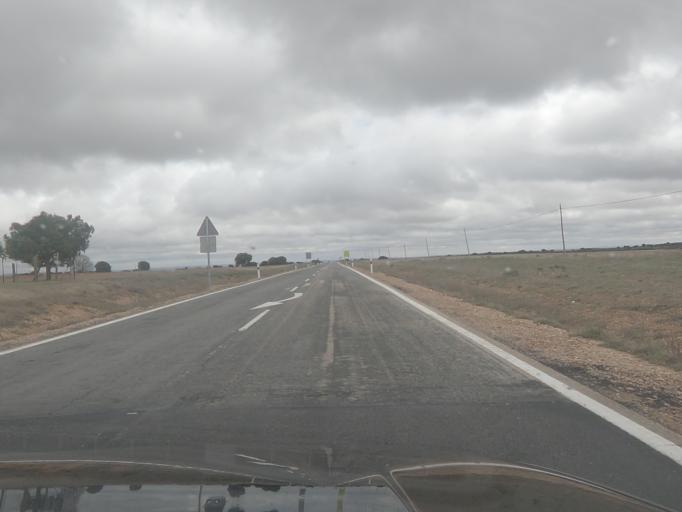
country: ES
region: Castille and Leon
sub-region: Provincia de Zamora
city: Perilla de Castro
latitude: 41.7447
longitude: -5.8382
